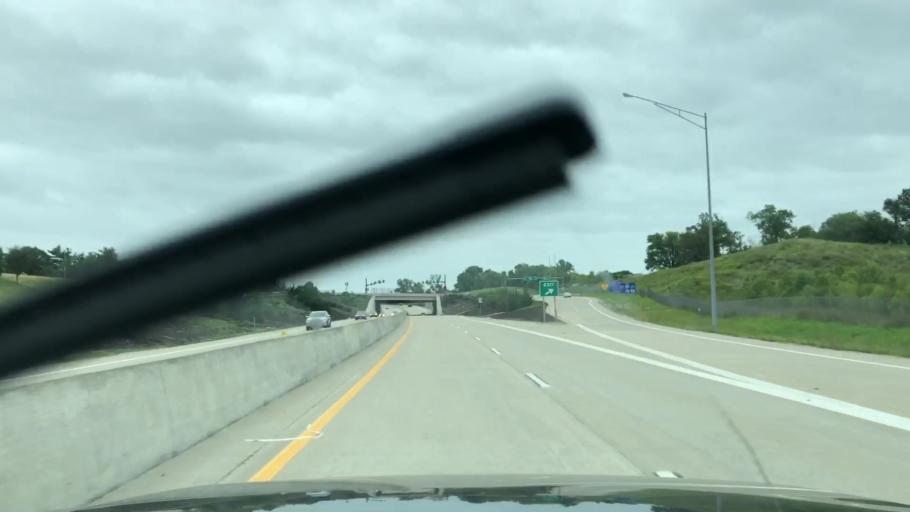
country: US
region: Missouri
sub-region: Saint Louis County
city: Town and Country
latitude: 38.6781
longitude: -90.4933
